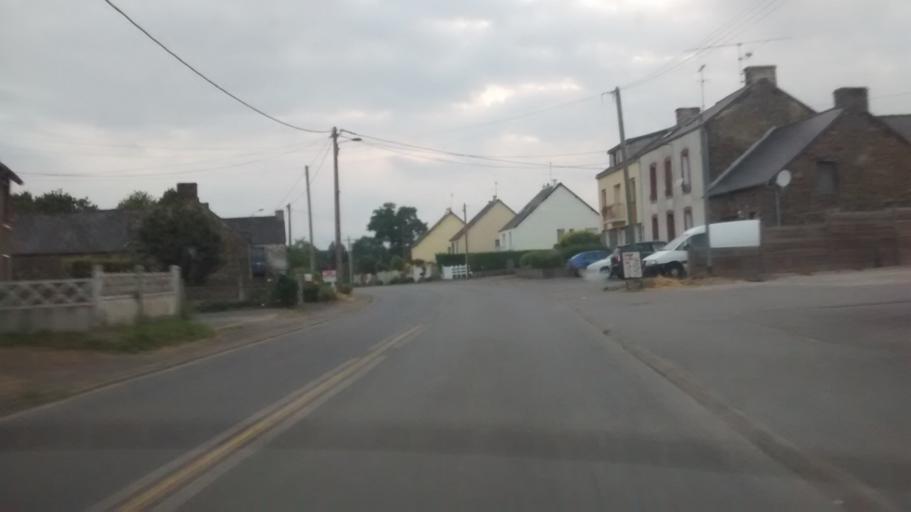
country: FR
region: Brittany
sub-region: Departement du Morbihan
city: Saint-Martin-sur-Oust
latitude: 47.7461
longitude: -2.2563
